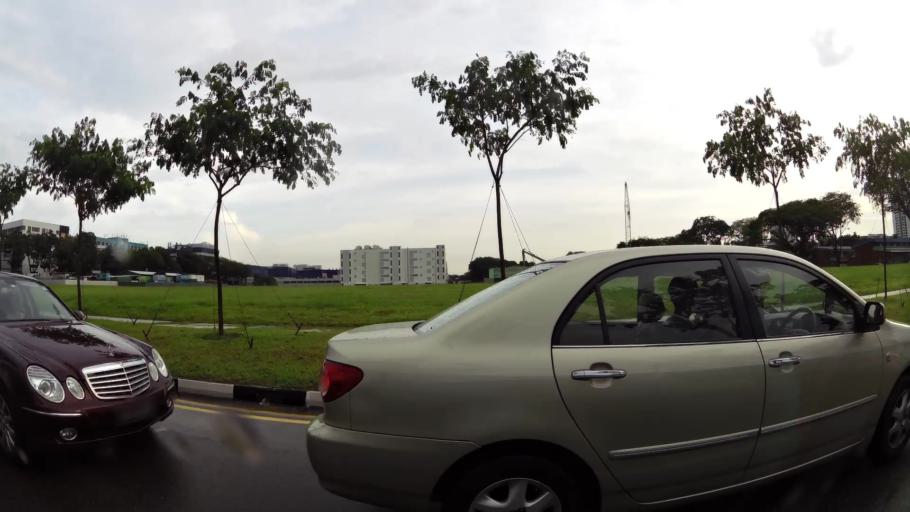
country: SG
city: Singapore
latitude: 1.3775
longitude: 103.8619
